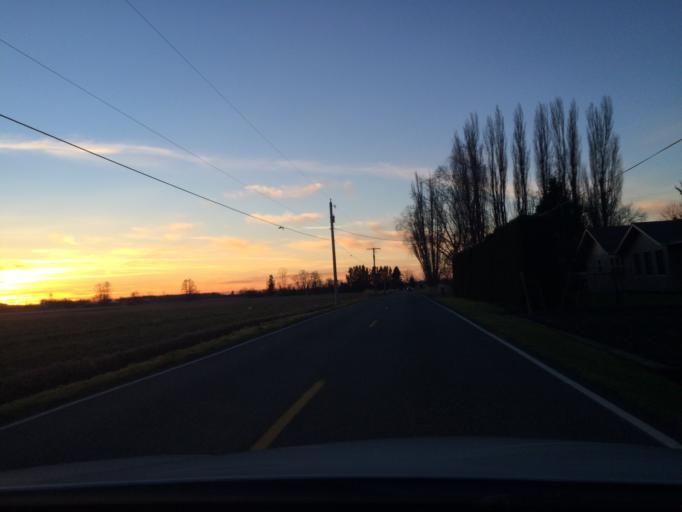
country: US
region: Washington
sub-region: Whatcom County
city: Nooksack
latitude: 48.9347
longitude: -122.3248
